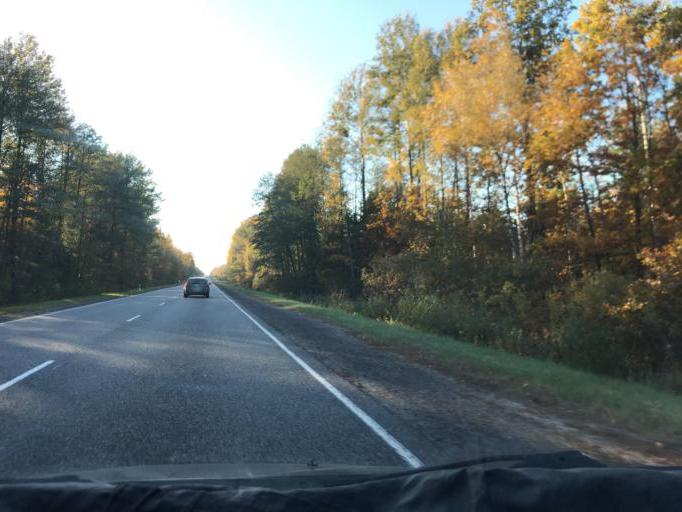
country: BY
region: Gomel
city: Zhytkavichy
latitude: 52.2740
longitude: 28.1395
